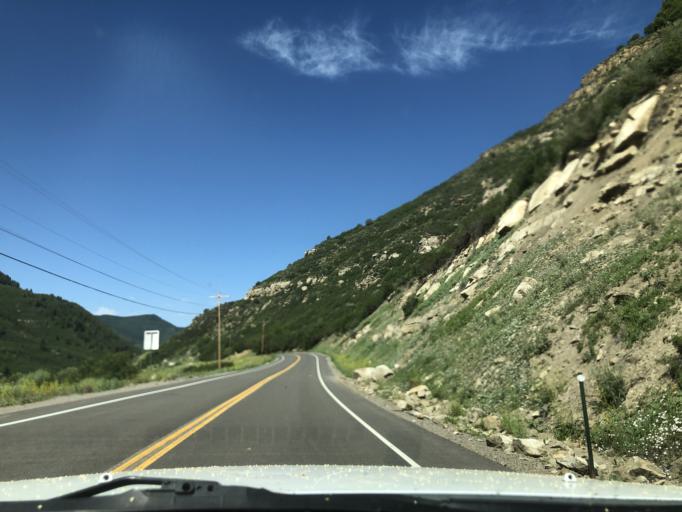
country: US
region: Colorado
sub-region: Delta County
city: Paonia
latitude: 38.9340
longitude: -107.3992
